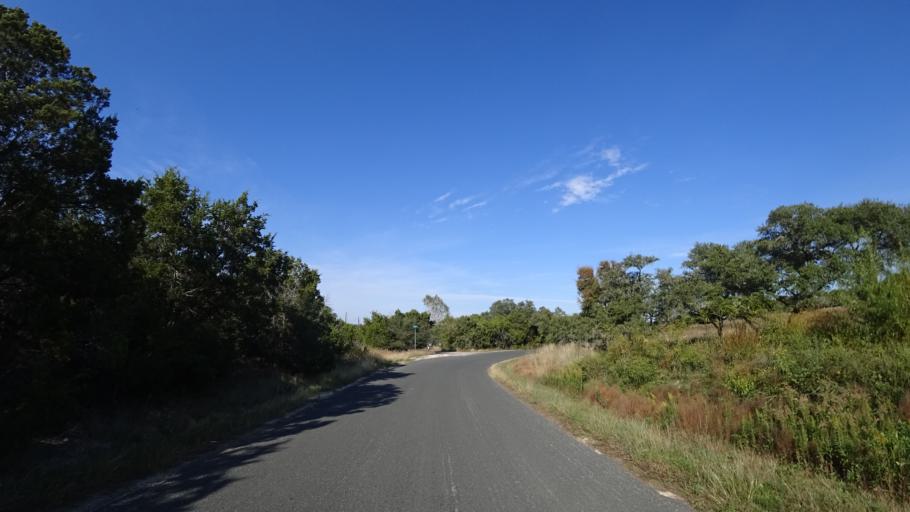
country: US
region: Texas
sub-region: Travis County
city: Bee Cave
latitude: 30.2339
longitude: -97.9316
